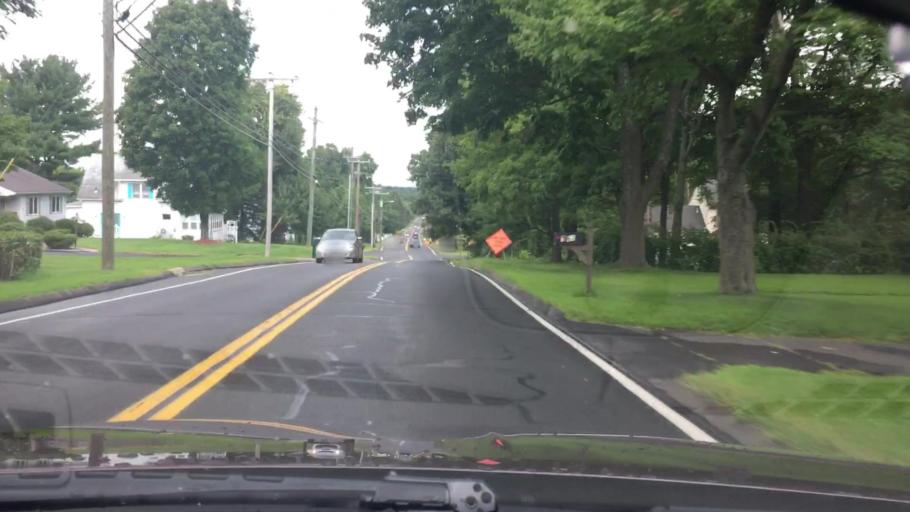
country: US
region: Connecticut
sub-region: Hartford County
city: Manchester
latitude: 41.7499
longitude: -72.5398
